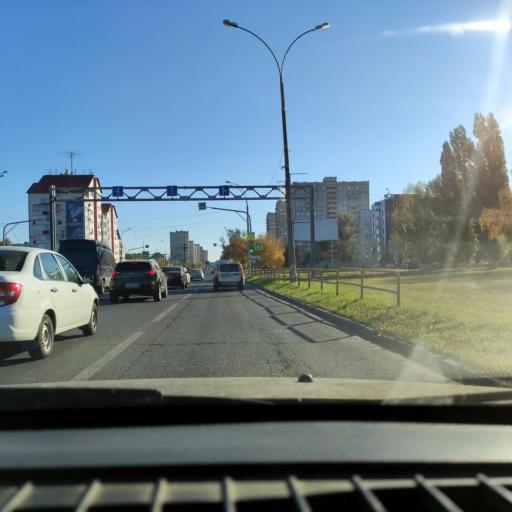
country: RU
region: Samara
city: Tol'yatti
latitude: 53.5150
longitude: 49.2766
